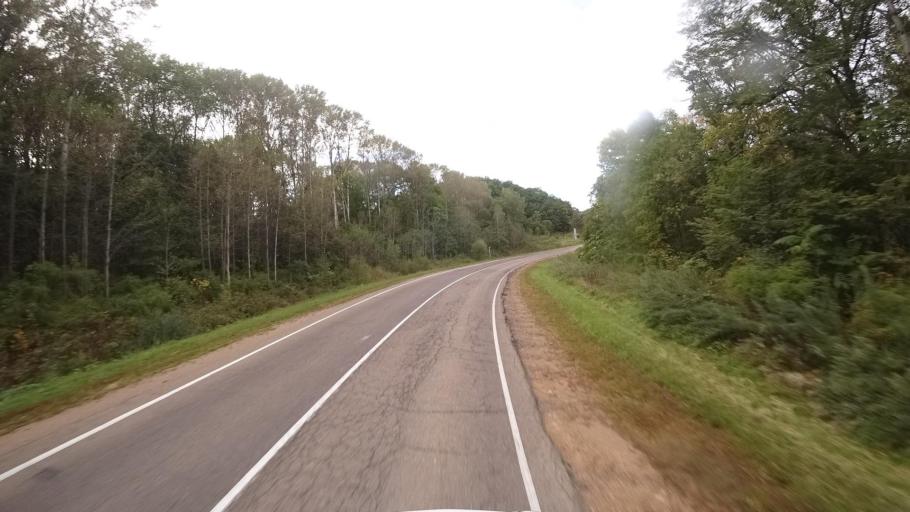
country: RU
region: Primorskiy
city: Yakovlevka
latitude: 44.4064
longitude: 133.4578
